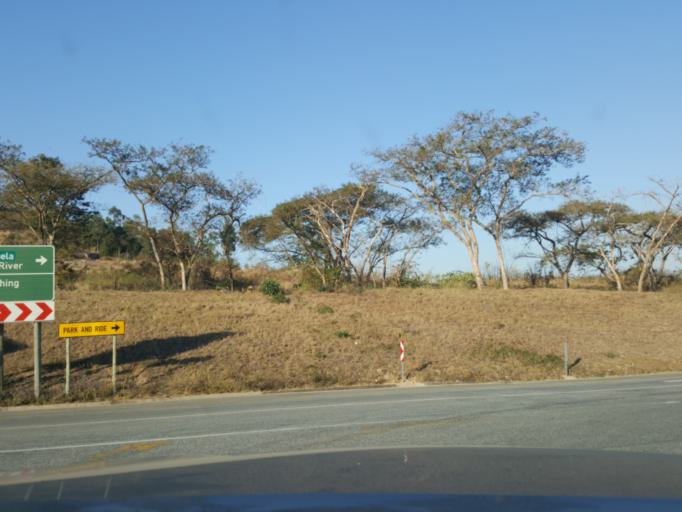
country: ZA
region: Mpumalanga
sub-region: Ehlanzeni District
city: Nelspruit
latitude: -25.4366
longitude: 30.9507
